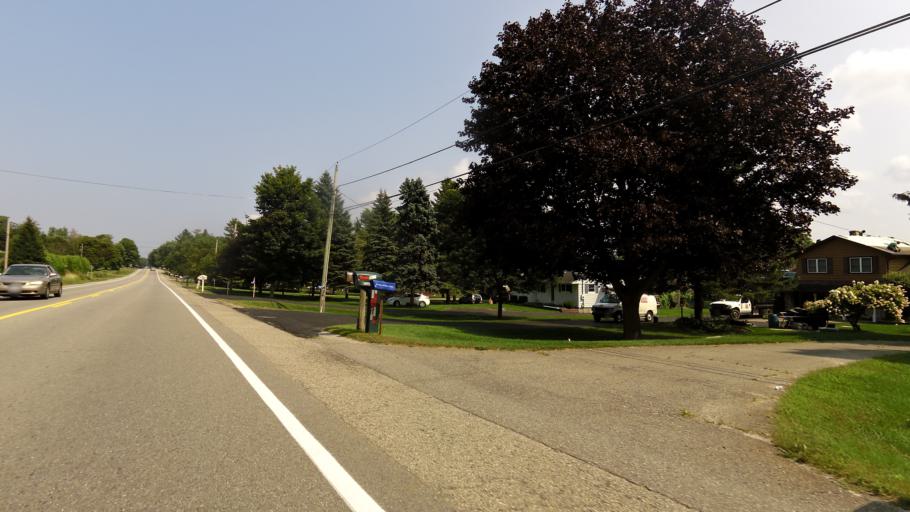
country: CA
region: Ontario
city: Brockville
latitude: 44.6267
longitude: -75.6256
